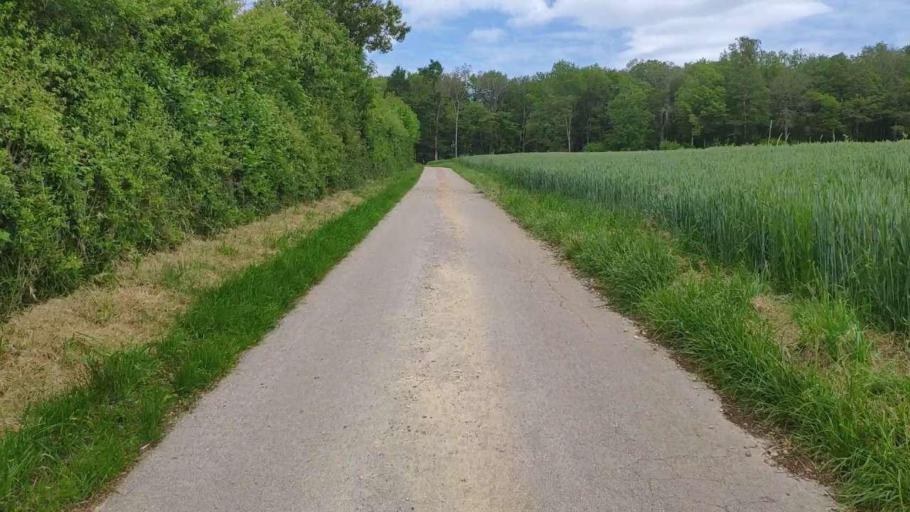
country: FR
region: Franche-Comte
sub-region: Departement du Jura
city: Poligny
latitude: 46.7696
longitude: 5.6558
